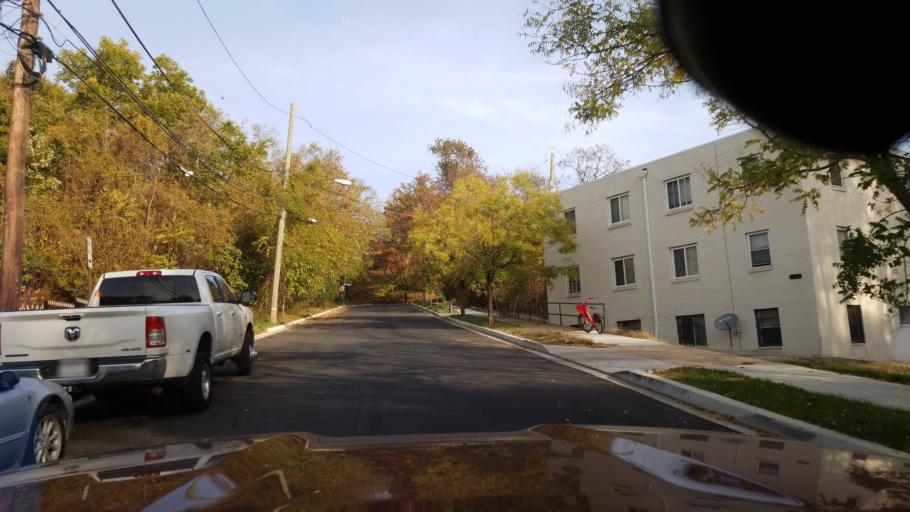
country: US
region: Maryland
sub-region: Prince George's County
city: Hillcrest Heights
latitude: 38.8542
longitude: -76.9828
